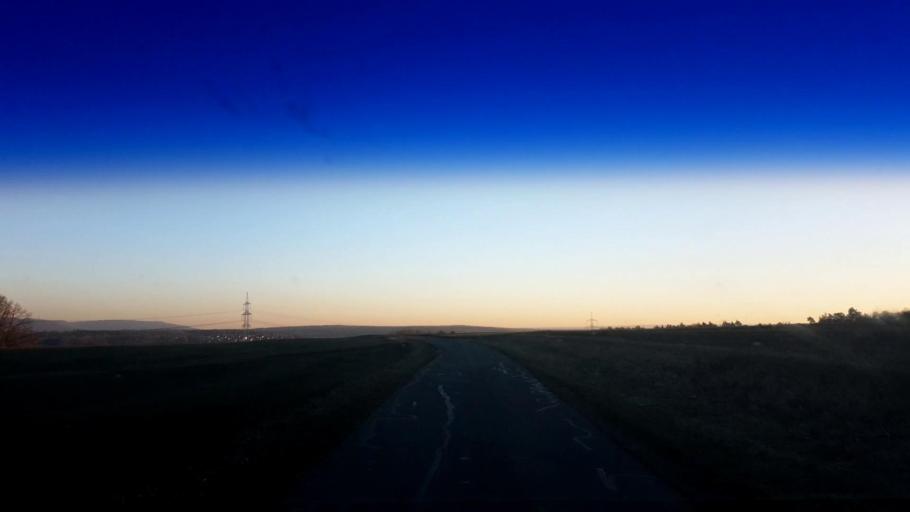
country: DE
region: Bavaria
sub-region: Upper Franconia
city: Memmelsdorf
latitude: 49.9518
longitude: 10.9467
